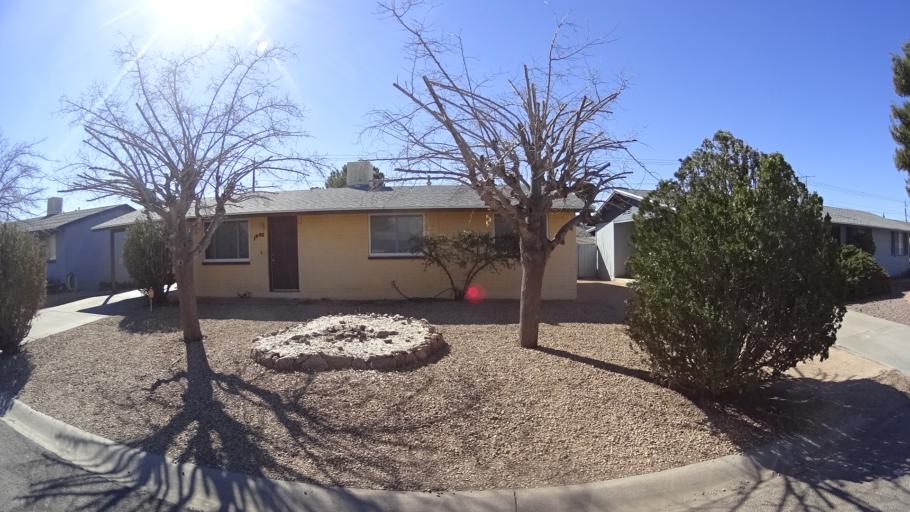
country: US
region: Arizona
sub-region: Mohave County
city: Kingman
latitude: 35.2111
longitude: -114.0334
